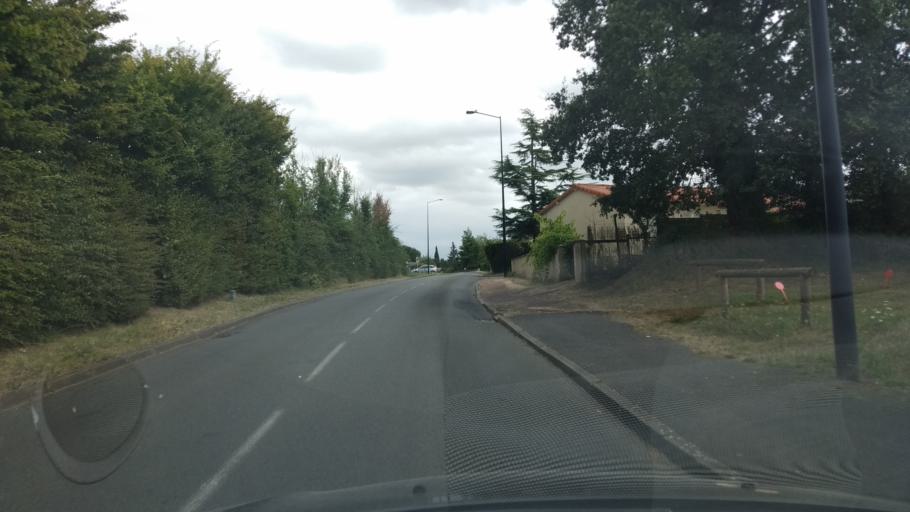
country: FR
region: Poitou-Charentes
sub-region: Departement de la Vienne
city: Smarves
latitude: 46.5089
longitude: 0.3561
